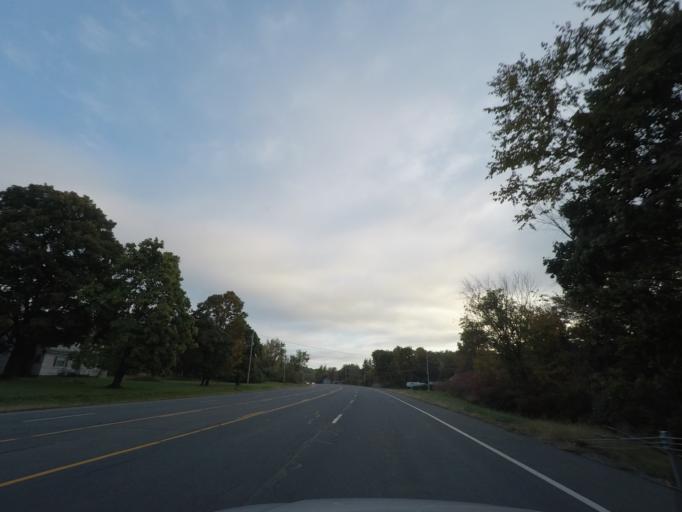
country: US
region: New York
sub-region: Rensselaer County
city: East Greenbush
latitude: 42.5370
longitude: -73.6788
